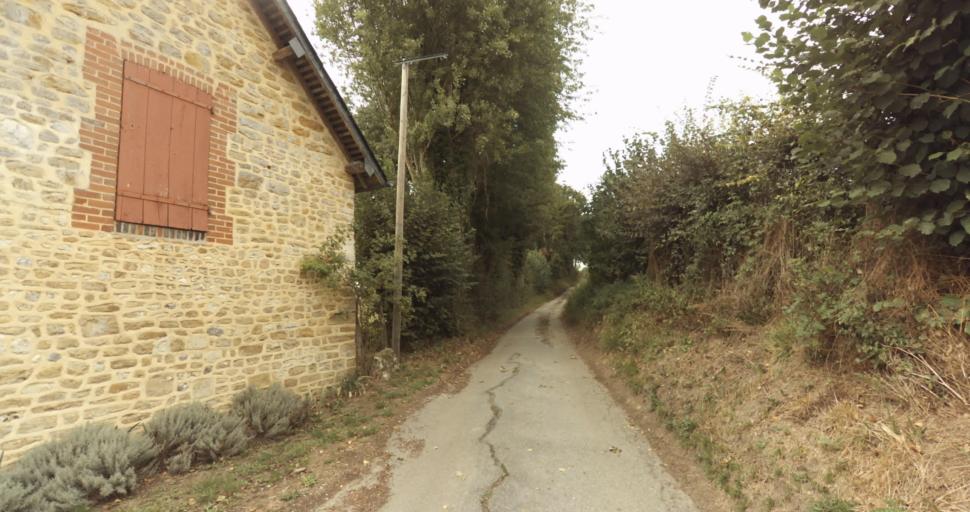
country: FR
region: Lower Normandy
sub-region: Departement de l'Orne
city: Gace
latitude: 48.8152
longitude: 0.2908
